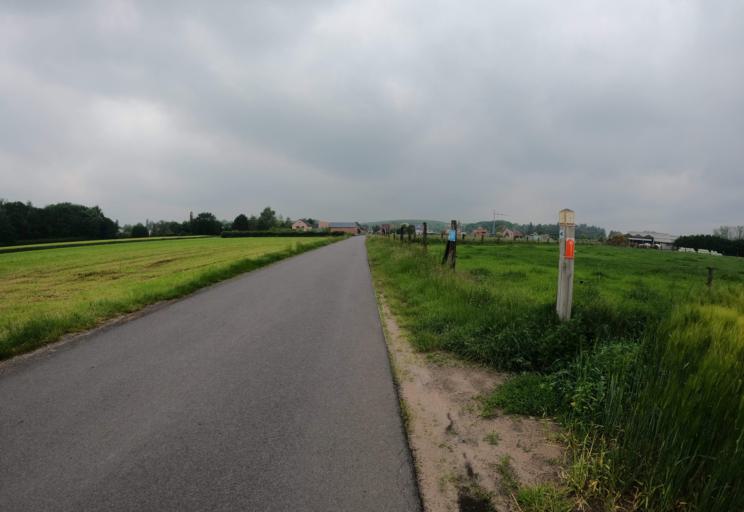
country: BE
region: Flanders
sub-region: Provincie Oost-Vlaanderen
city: Berlare
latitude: 51.0320
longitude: 4.0126
